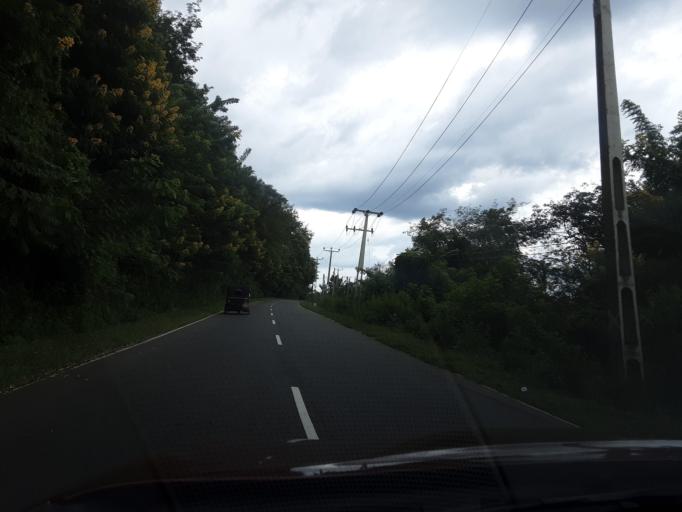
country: LK
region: Uva
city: Monaragala
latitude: 6.9047
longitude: 81.2124
